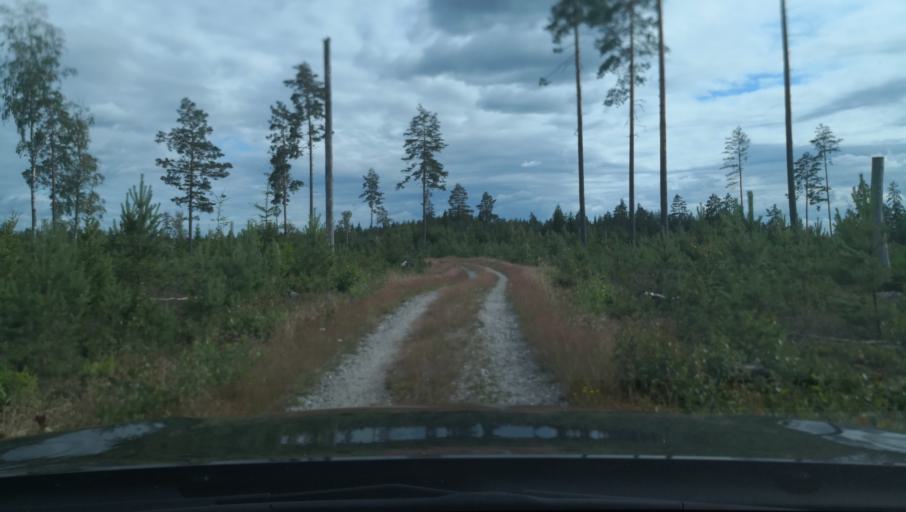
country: SE
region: Vaestmanland
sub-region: Hallstahammars Kommun
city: Hallstahammar
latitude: 59.6494
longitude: 16.0852
